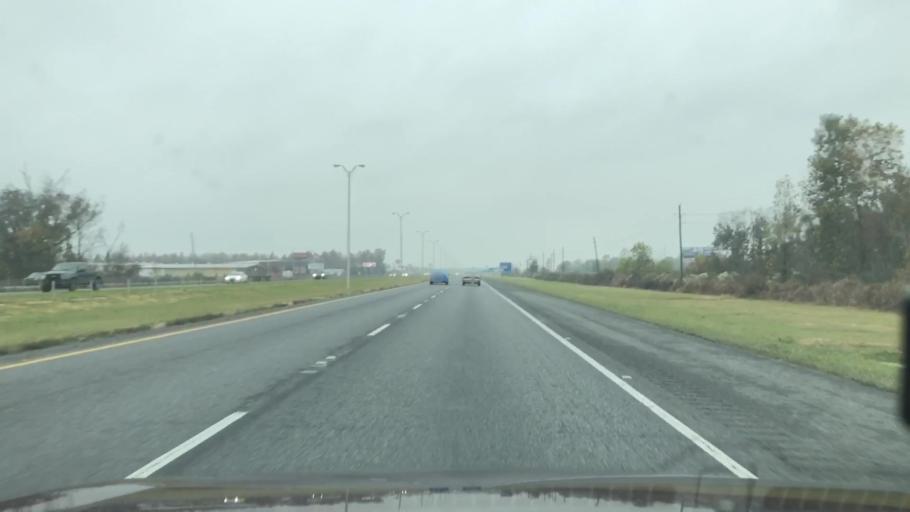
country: US
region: Louisiana
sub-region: Ouachita Parish
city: Lakeshore
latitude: 32.4927
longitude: -92.0326
